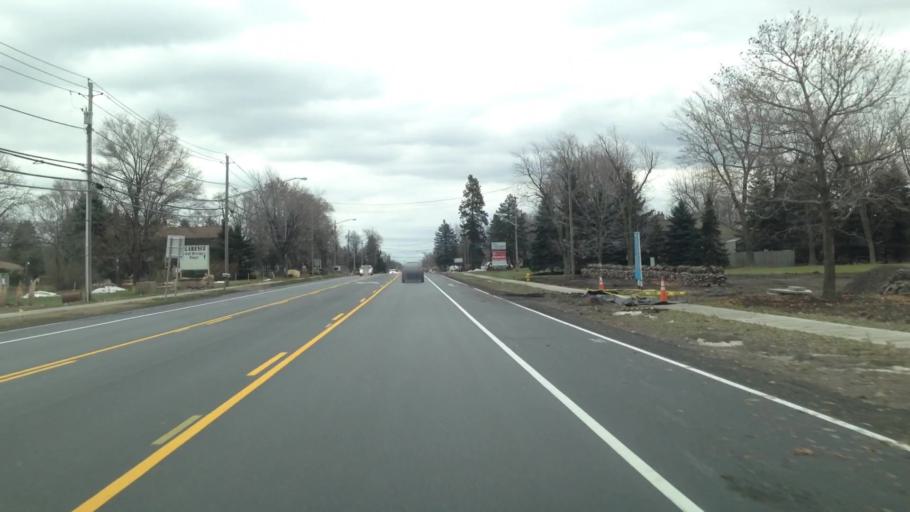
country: US
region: New York
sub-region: Erie County
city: Harris Hill
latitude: 42.9678
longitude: -78.6562
